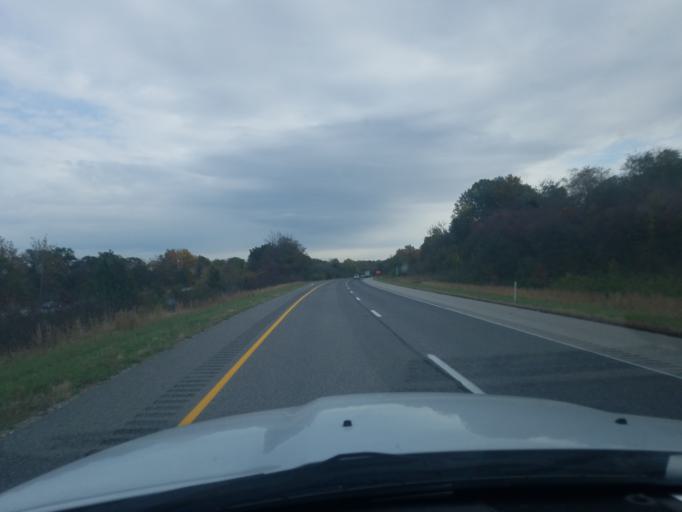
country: US
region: Indiana
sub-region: Warrick County
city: Boonville
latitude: 38.2015
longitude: -87.2384
